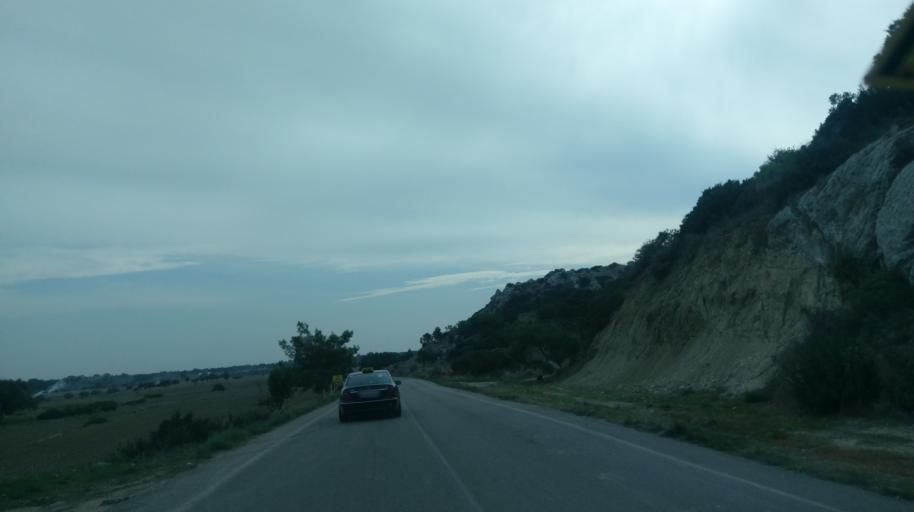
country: CY
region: Ammochostos
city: Leonarisso
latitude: 35.4446
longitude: 34.1362
